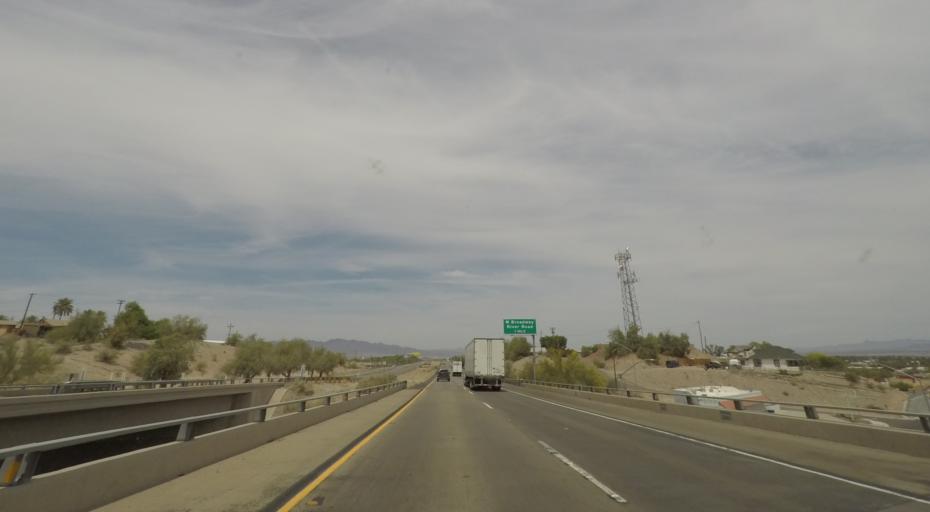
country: US
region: California
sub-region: San Bernardino County
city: Needles
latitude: 34.8393
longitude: -114.6112
